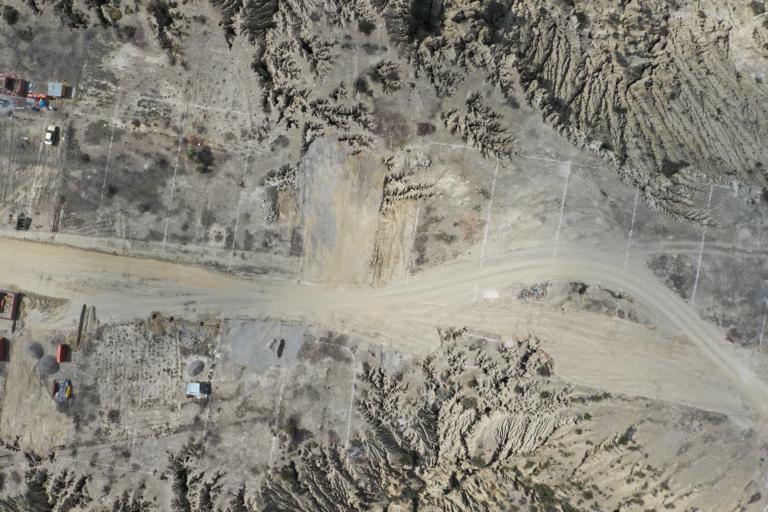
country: BO
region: La Paz
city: La Paz
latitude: -16.5649
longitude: -68.1205
